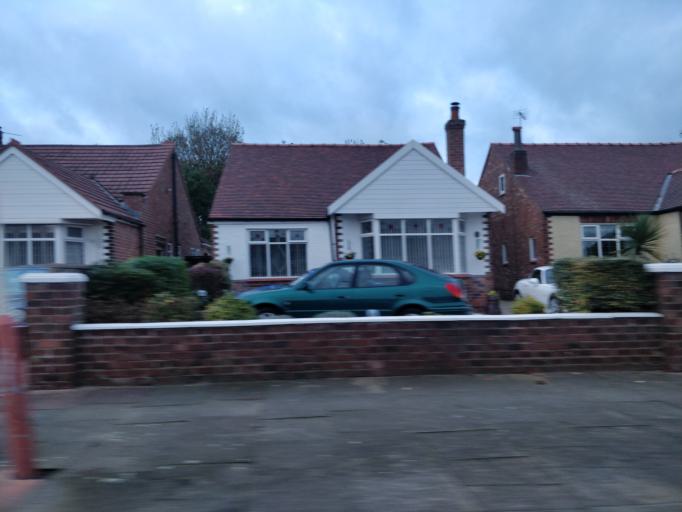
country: GB
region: England
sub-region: Sefton
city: Southport
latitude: 53.6650
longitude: -2.9749
